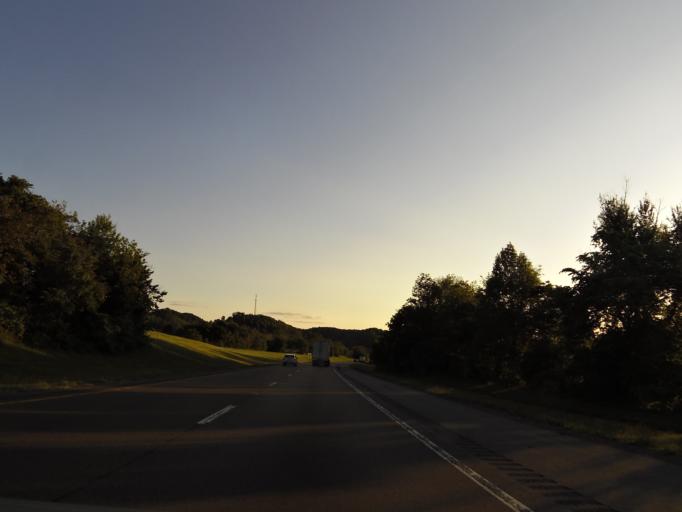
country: US
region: Tennessee
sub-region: Washington County
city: Fall Branch
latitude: 36.4049
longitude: -82.6074
